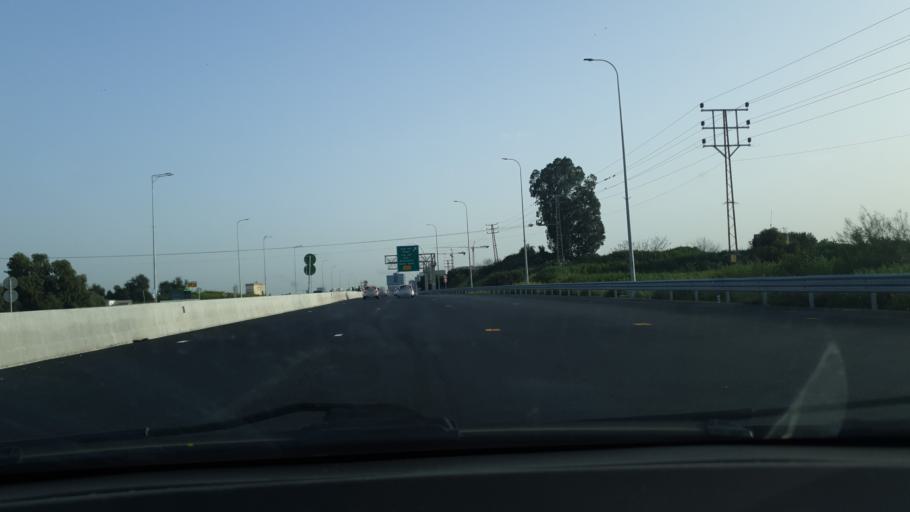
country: IL
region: Central District
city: Ra'anana
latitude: 32.2093
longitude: 34.8837
